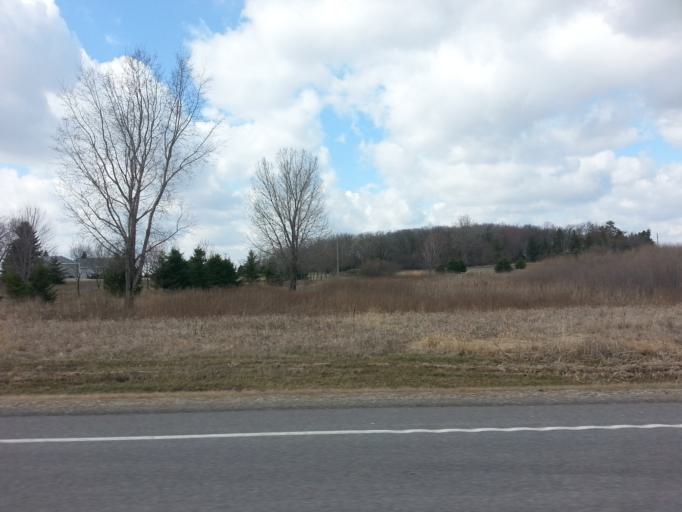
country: US
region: Minnesota
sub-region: Dodge County
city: Mantorville
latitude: 44.0803
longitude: -92.6939
